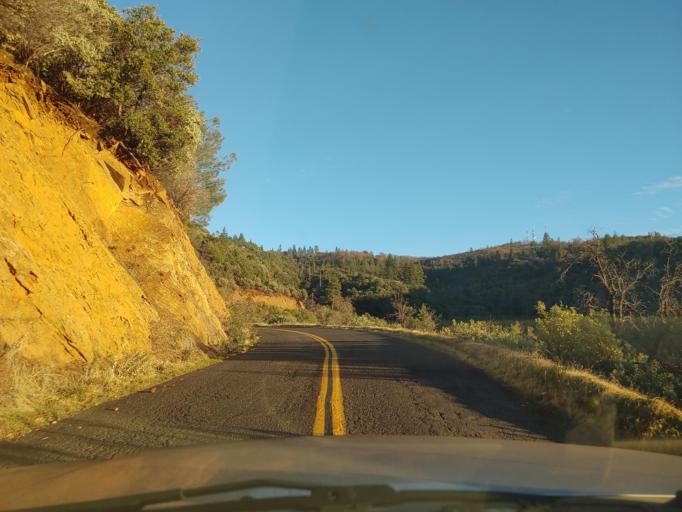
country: US
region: California
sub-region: Tuolumne County
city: Columbia
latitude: 38.0406
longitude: -120.3629
